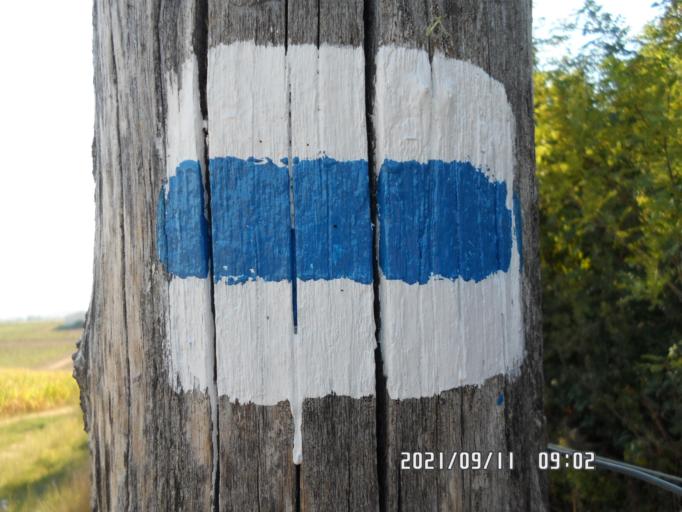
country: HU
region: Zala
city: Zalaegerszeg
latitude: 46.7043
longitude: 16.7491
